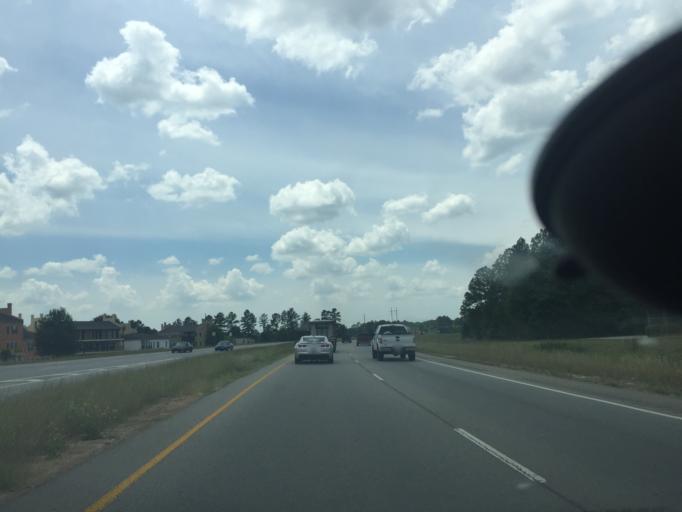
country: US
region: Georgia
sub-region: Bulloch County
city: Statesboro
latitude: 32.4069
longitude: -81.7648
